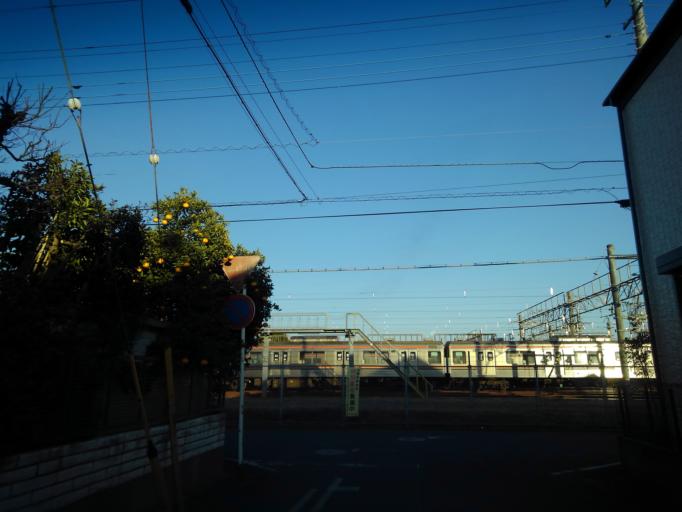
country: JP
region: Saitama
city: Oi
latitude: 35.8022
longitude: 139.5200
